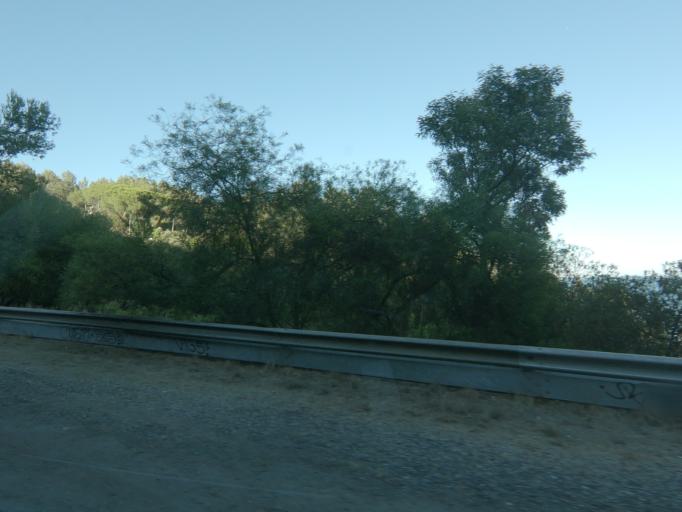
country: PT
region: Setubal
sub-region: Setubal
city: Setubal
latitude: 38.5113
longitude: -8.9207
